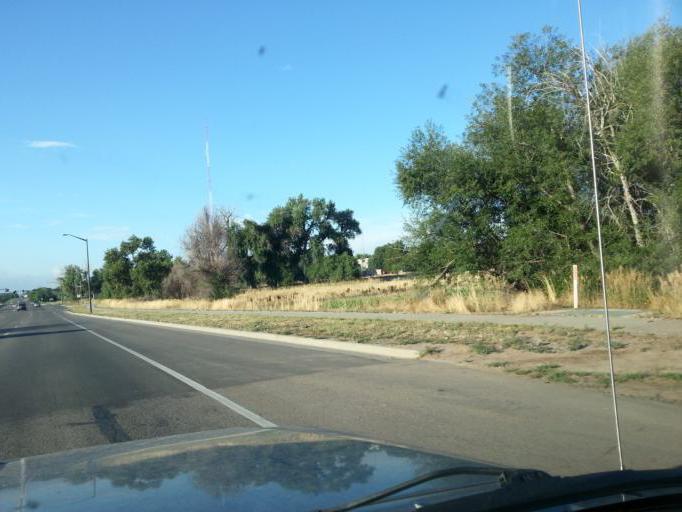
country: US
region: Colorado
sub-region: Larimer County
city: Loveland
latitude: 40.3950
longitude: -105.0969
